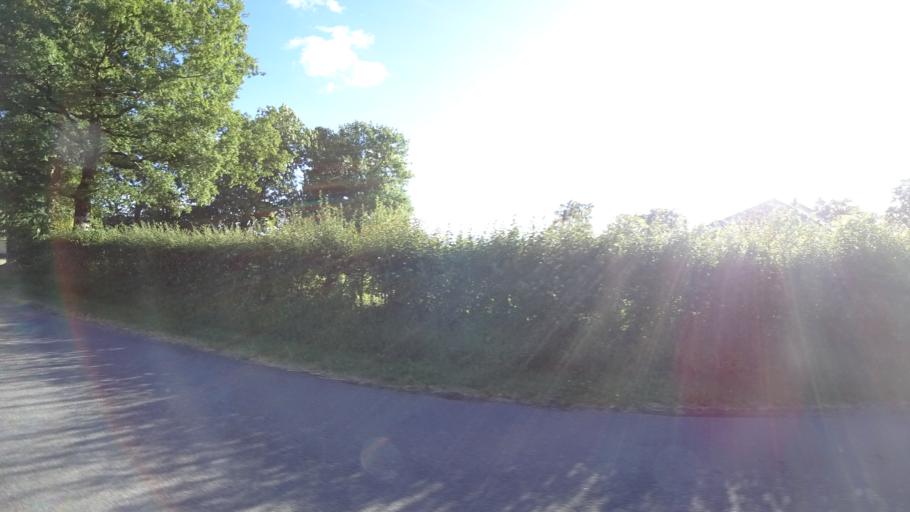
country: FR
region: Midi-Pyrenees
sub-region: Departement de l'Aveyron
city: Pont-de-Salars
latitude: 44.3116
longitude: 2.7583
